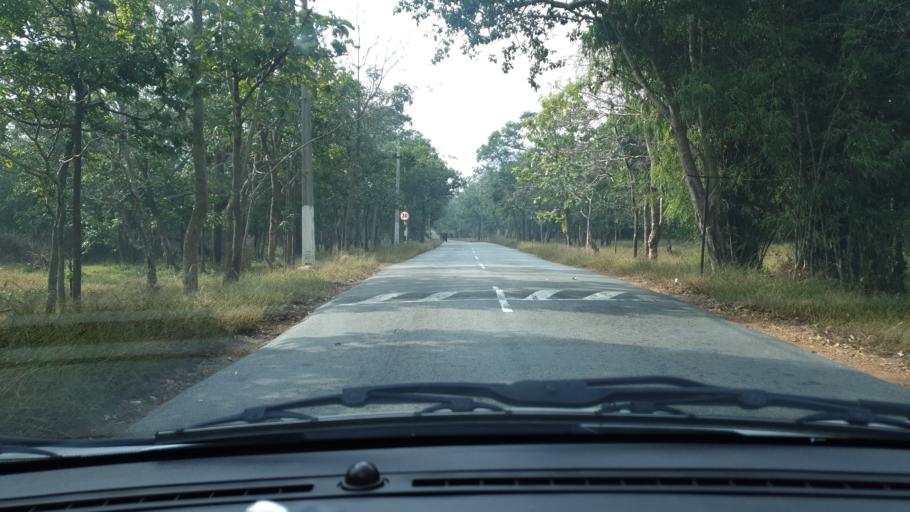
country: IN
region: Andhra Pradesh
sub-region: Kurnool
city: Srisailam
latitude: 16.2845
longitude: 78.7273
